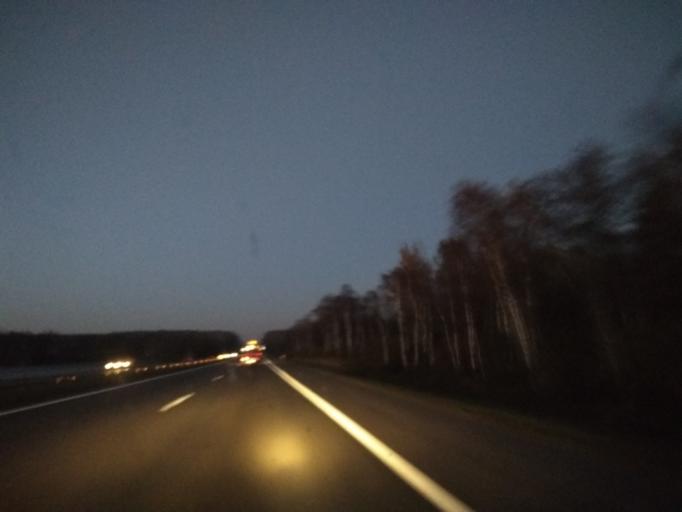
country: BY
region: Minsk
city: Enyerhyetykaw
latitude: 53.6260
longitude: 27.0566
